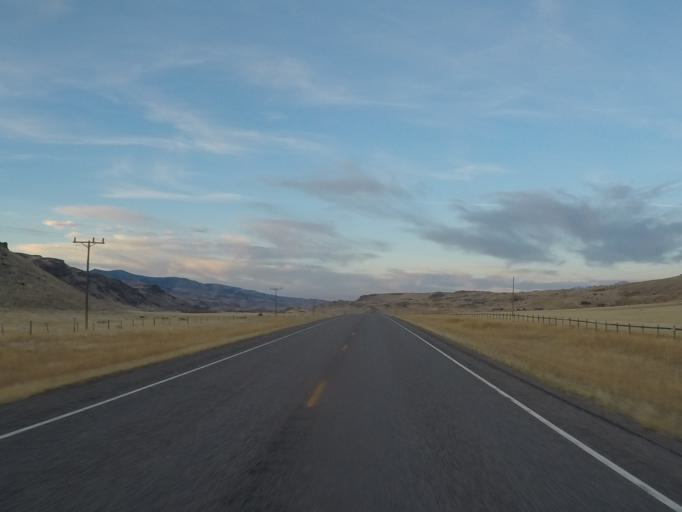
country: US
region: Montana
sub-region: Gallatin County
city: Bozeman
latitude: 45.2197
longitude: -110.8838
